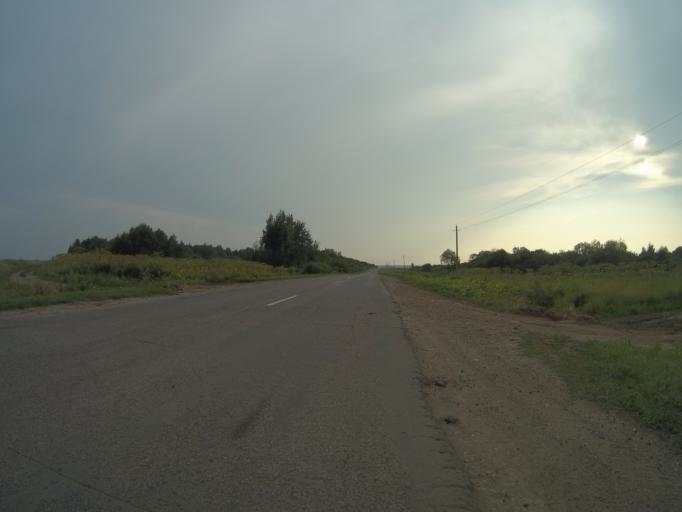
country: RU
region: Ivanovo
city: Gavrilov Posad
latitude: 56.3442
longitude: 40.1426
